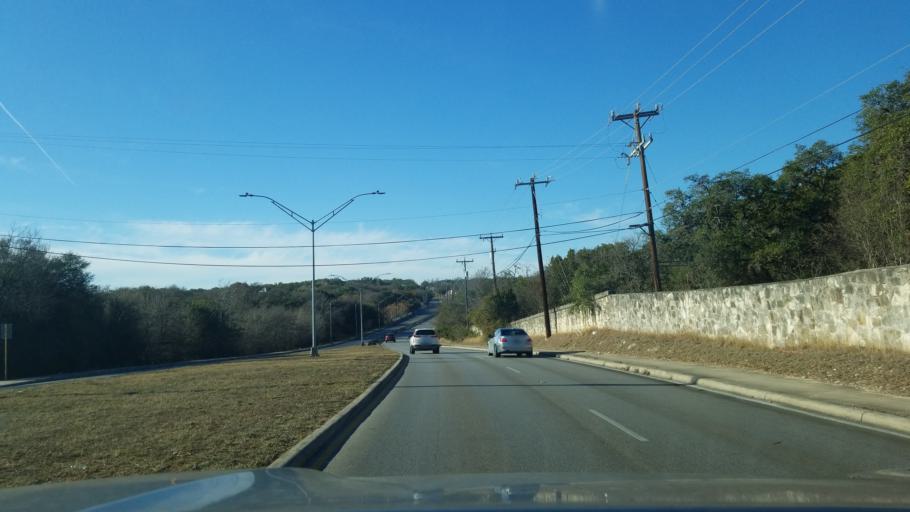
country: US
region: Texas
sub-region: Bexar County
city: Shavano Park
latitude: 29.5718
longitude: -98.5504
